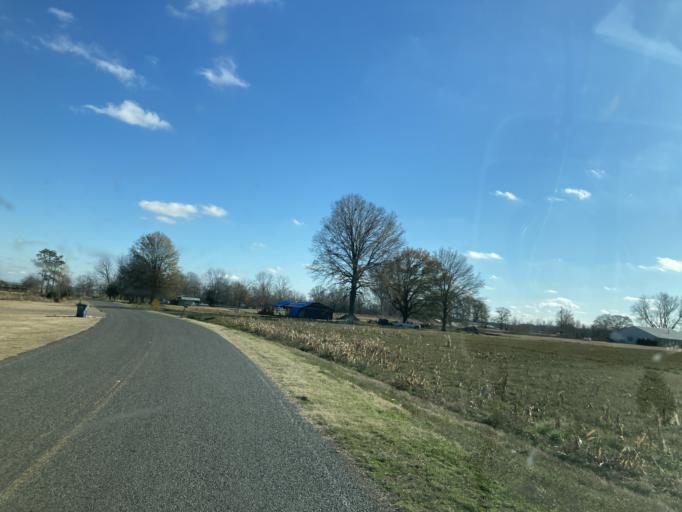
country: US
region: Mississippi
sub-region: Yazoo County
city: Yazoo City
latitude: 32.9272
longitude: -90.4711
